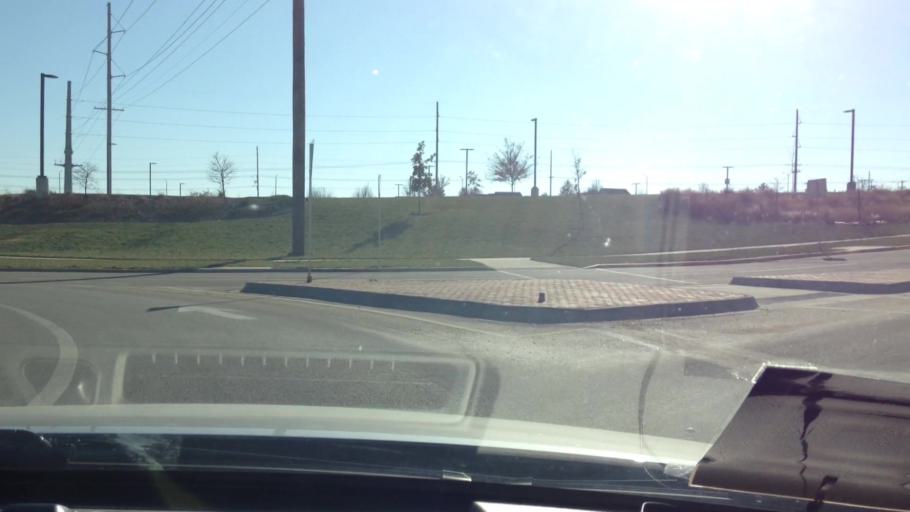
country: US
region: Kansas
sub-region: Johnson County
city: Olathe
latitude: 38.8857
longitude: -94.8508
